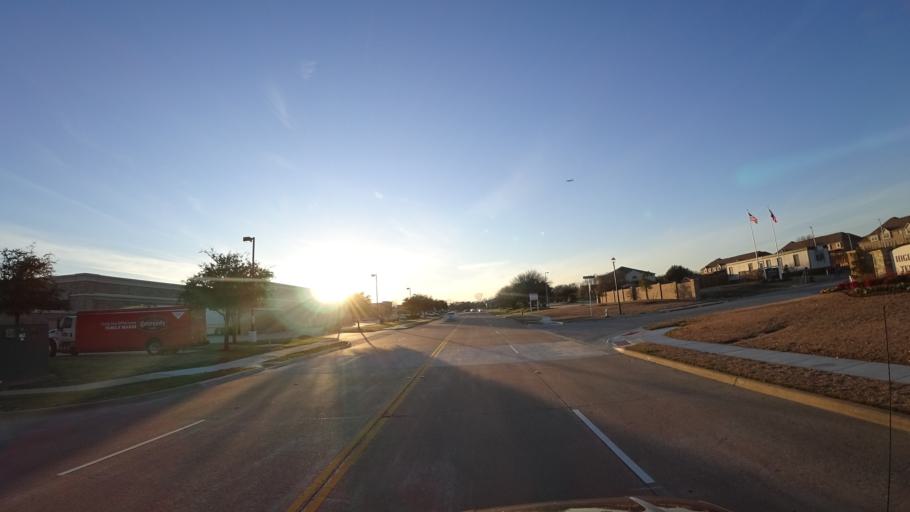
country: US
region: Texas
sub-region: Dallas County
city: Coppell
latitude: 32.9894
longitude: -96.9909
